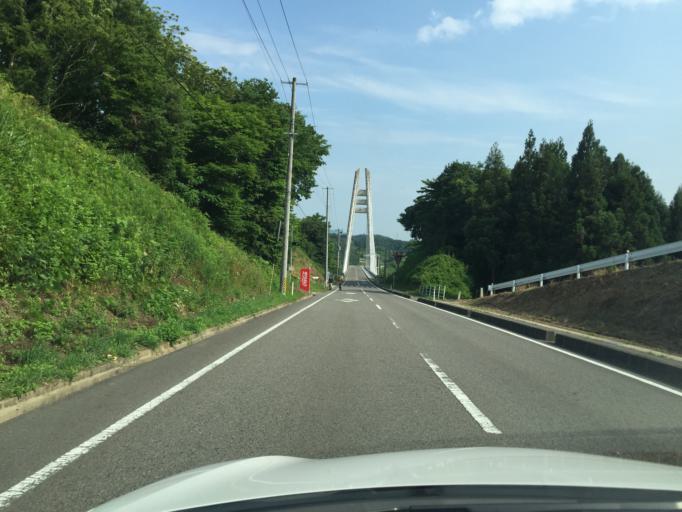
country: JP
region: Fukushima
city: Miharu
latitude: 37.4107
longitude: 140.4852
